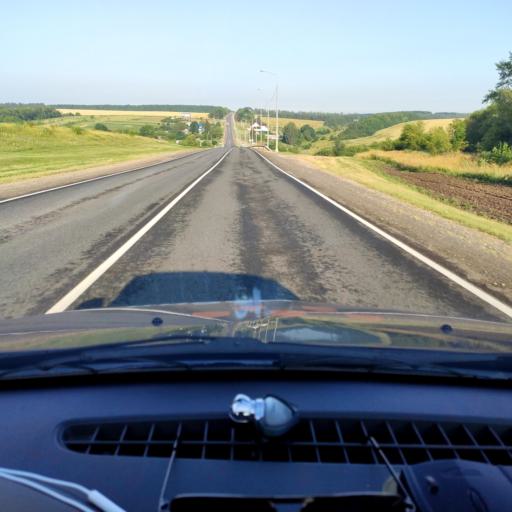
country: RU
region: Orjol
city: Livny
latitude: 52.4284
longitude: 37.7811
